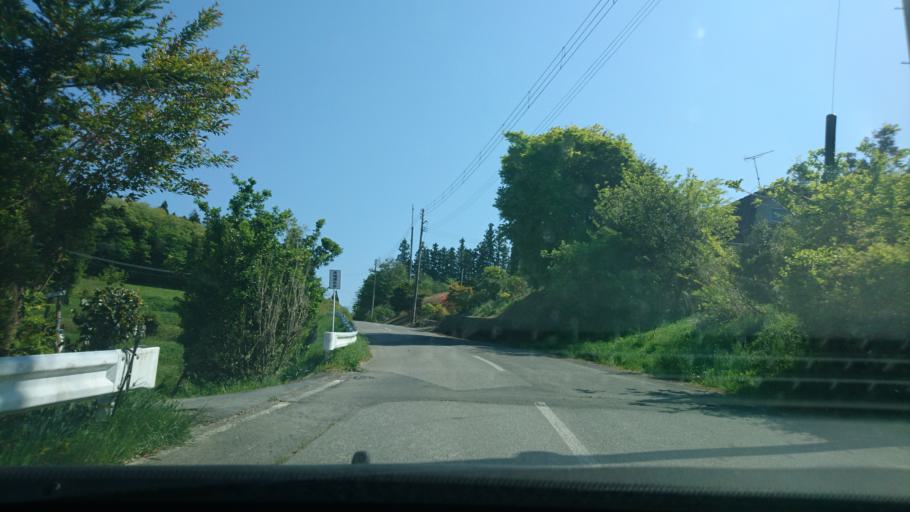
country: JP
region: Iwate
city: Ichinoseki
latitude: 38.9257
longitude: 141.2772
